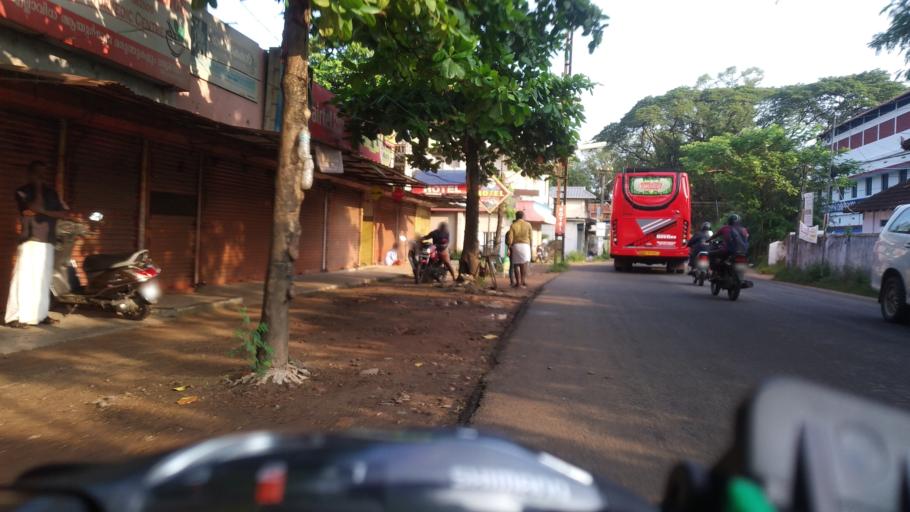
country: IN
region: Kerala
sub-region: Ernakulam
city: Elur
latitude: 10.0720
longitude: 76.2118
